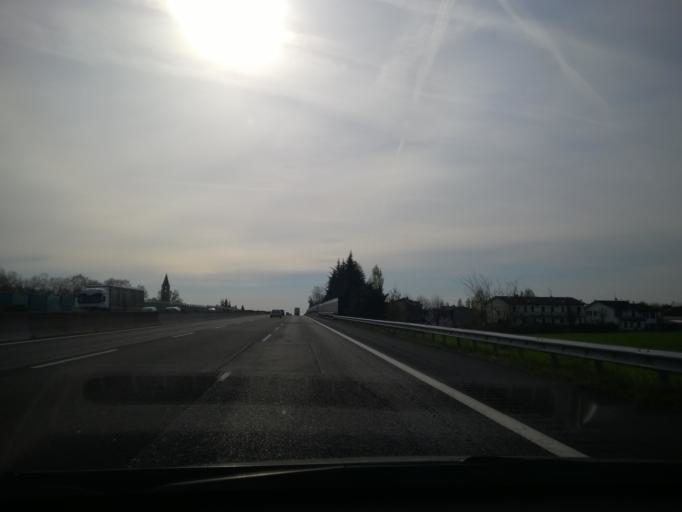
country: IT
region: Emilia-Romagna
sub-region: Forli-Cesena
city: Forli
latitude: 44.2685
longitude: 12.0445
